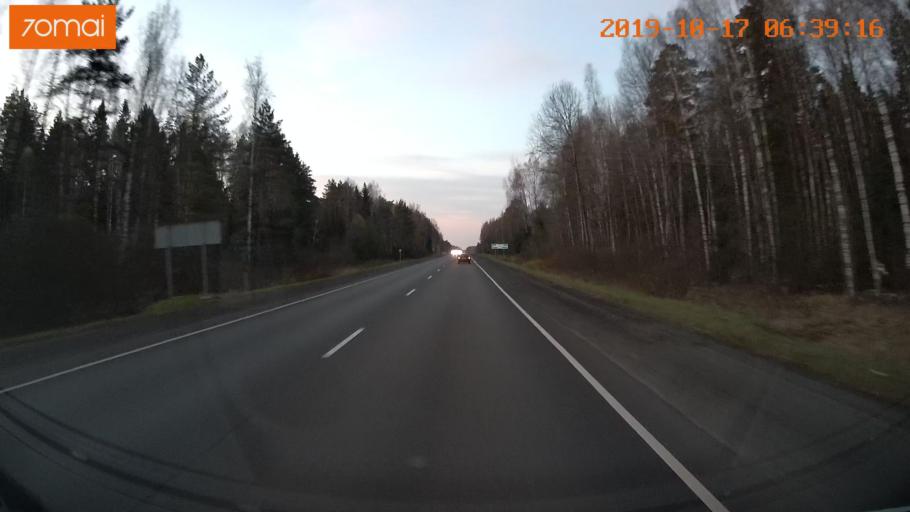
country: RU
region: Ivanovo
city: Novoye Leushino
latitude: 56.6453
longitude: 40.5803
